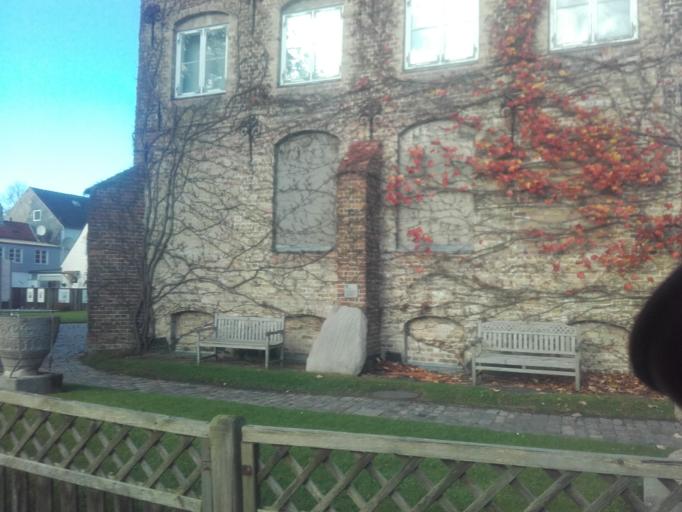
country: DE
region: Schleswig-Holstein
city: Busdorf
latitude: 54.5054
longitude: 9.5421
